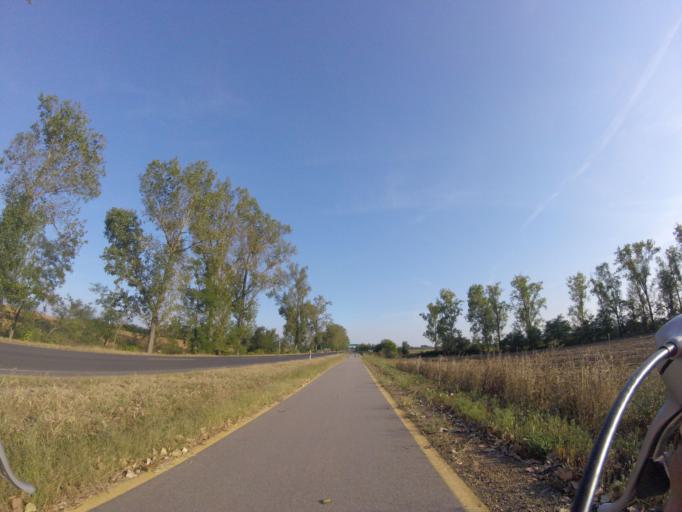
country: HU
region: Szabolcs-Szatmar-Bereg
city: Tiszanagyfalu
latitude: 48.0905
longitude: 21.4957
